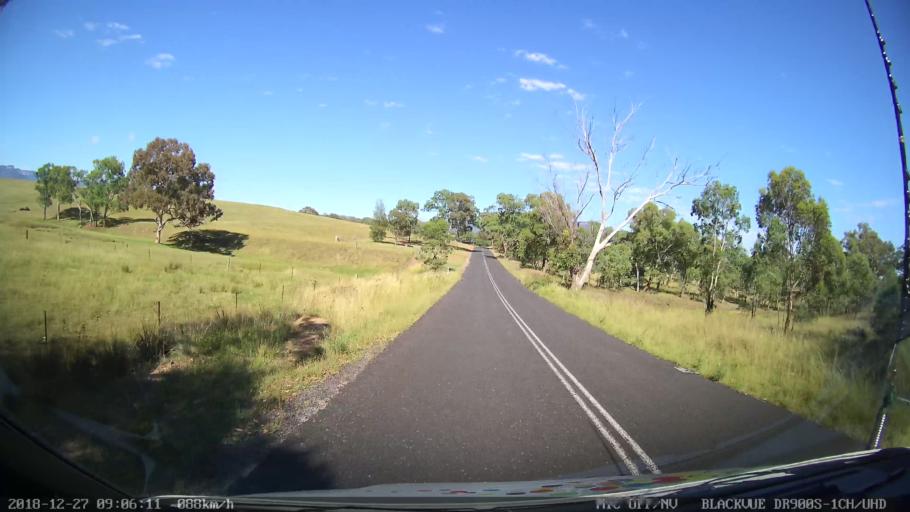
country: AU
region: New South Wales
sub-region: Lithgow
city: Portland
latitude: -33.1200
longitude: 150.1702
